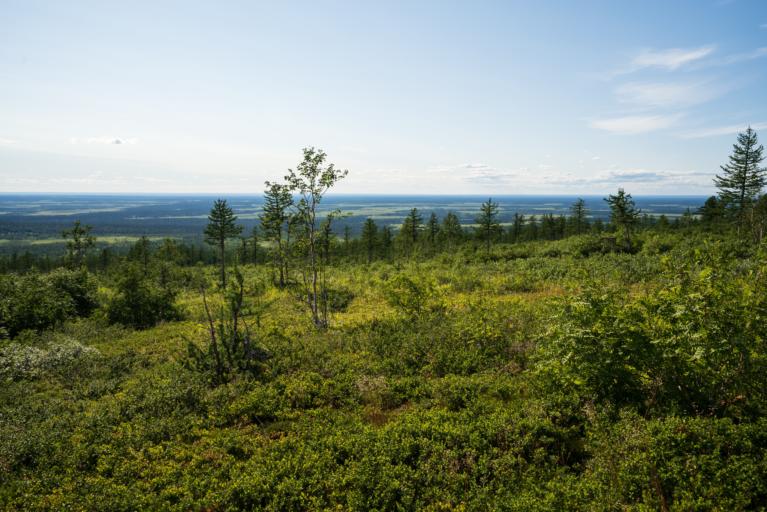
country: RU
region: Komi Republic
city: Synya
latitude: 64.7669
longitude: 58.8340
